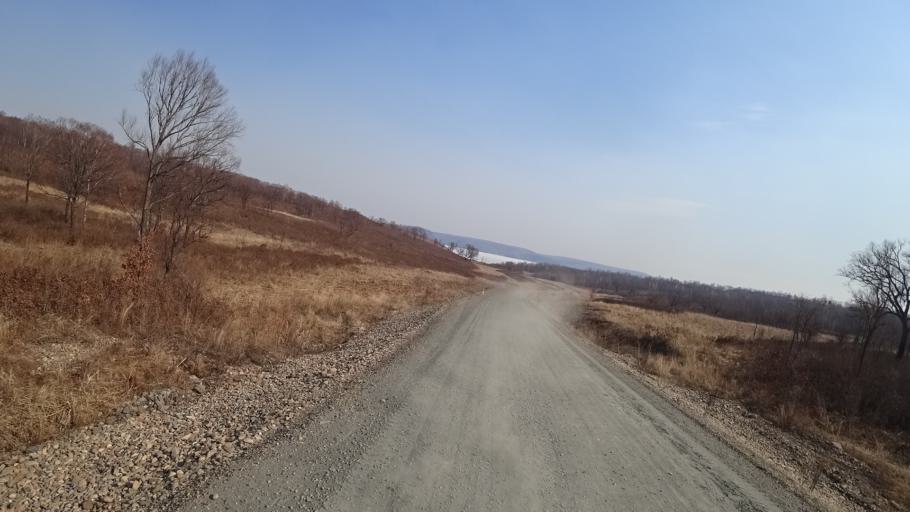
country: RU
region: Amur
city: Novobureyskiy
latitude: 49.8258
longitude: 129.9943
